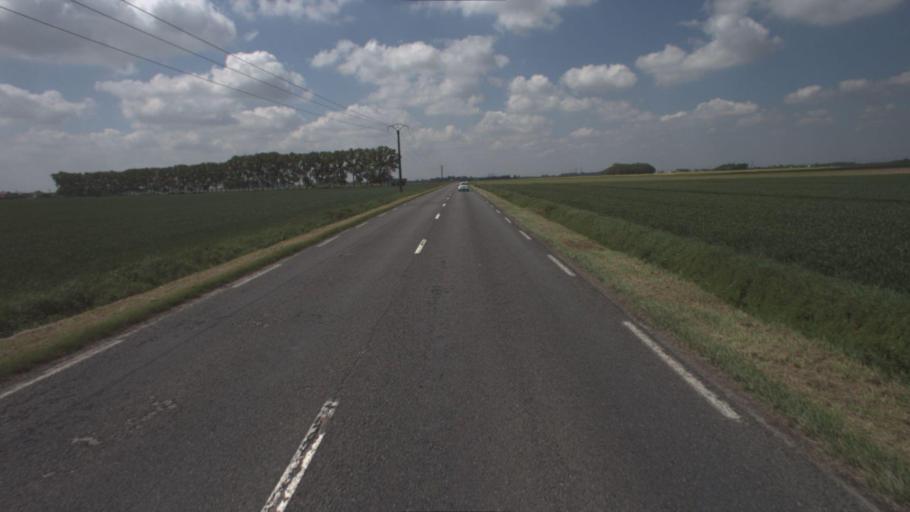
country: FR
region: Ile-de-France
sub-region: Departement de Seine-et-Marne
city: Guignes
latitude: 48.6241
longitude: 2.7662
